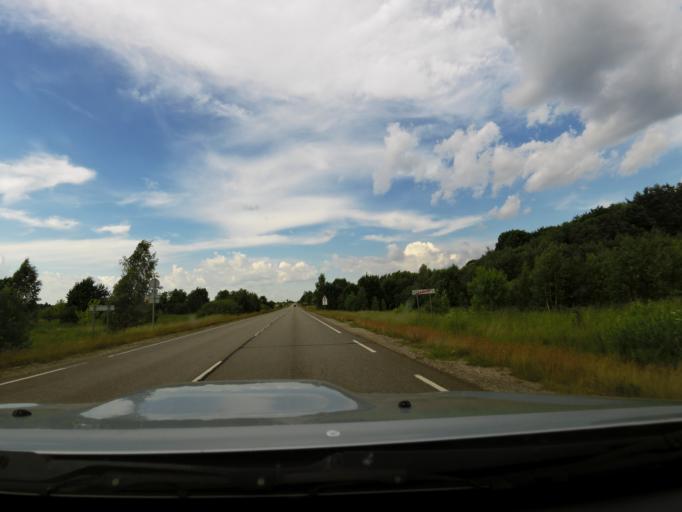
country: LT
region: Vilnius County
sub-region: Vilniaus Rajonas
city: Vievis
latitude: 54.8181
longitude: 24.9195
